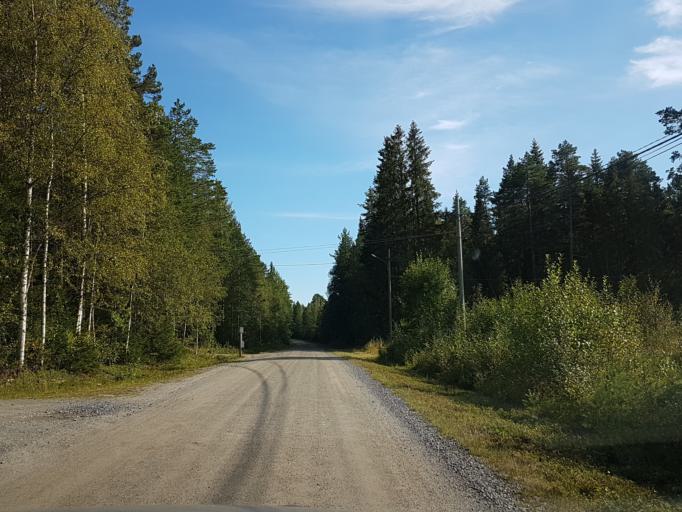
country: SE
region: Vaesterbotten
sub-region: Robertsfors Kommun
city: Robertsfors
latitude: 64.0547
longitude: 20.8706
